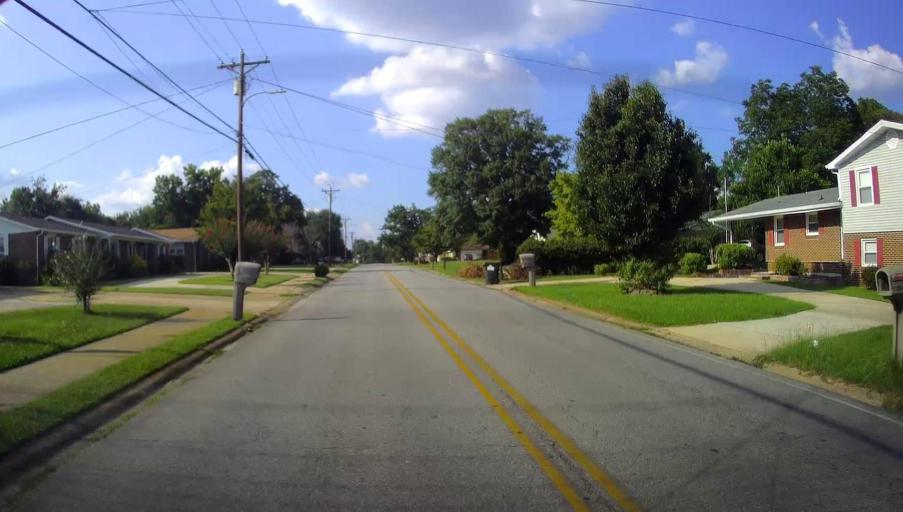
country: US
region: Georgia
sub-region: Houston County
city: Warner Robins
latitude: 32.5963
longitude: -83.6368
